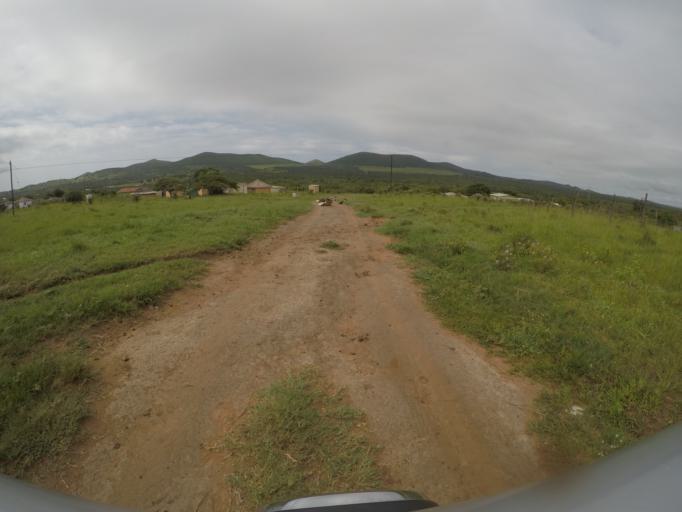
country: ZA
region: KwaZulu-Natal
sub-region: uThungulu District Municipality
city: Empangeni
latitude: -28.6155
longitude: 31.8460
